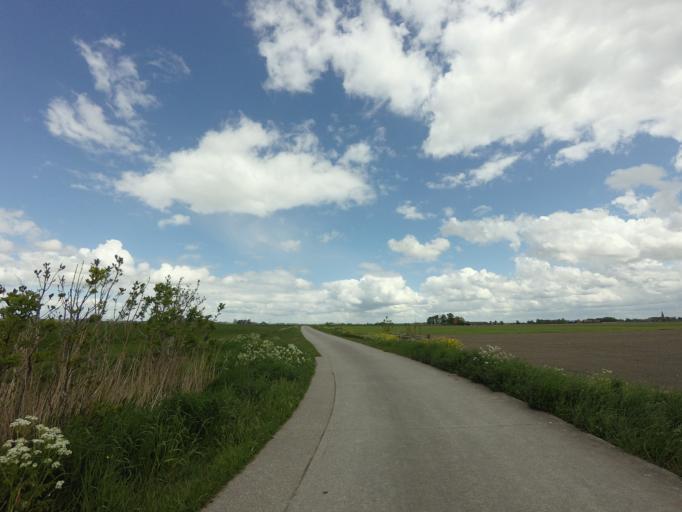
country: NL
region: Friesland
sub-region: Sudwest Fryslan
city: Bolsward
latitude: 53.0264
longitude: 5.5046
